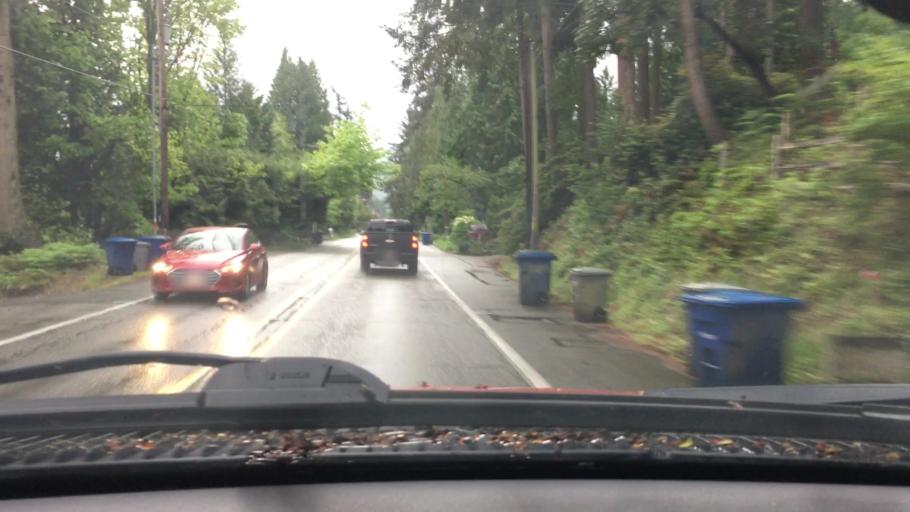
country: US
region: Washington
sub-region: King County
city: West Lake Sammamish
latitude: 47.5919
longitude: -122.1122
